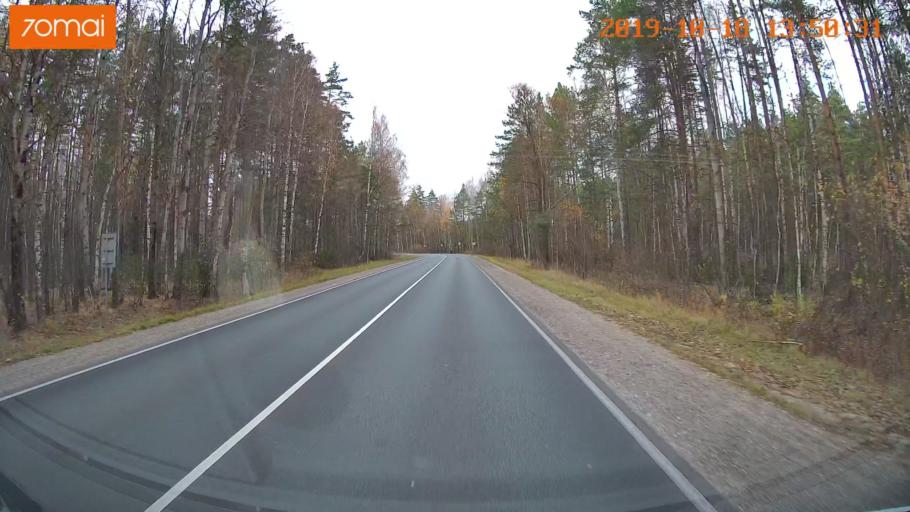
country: RU
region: Moskovskaya
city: Radovitskiy
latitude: 55.0071
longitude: 39.9704
